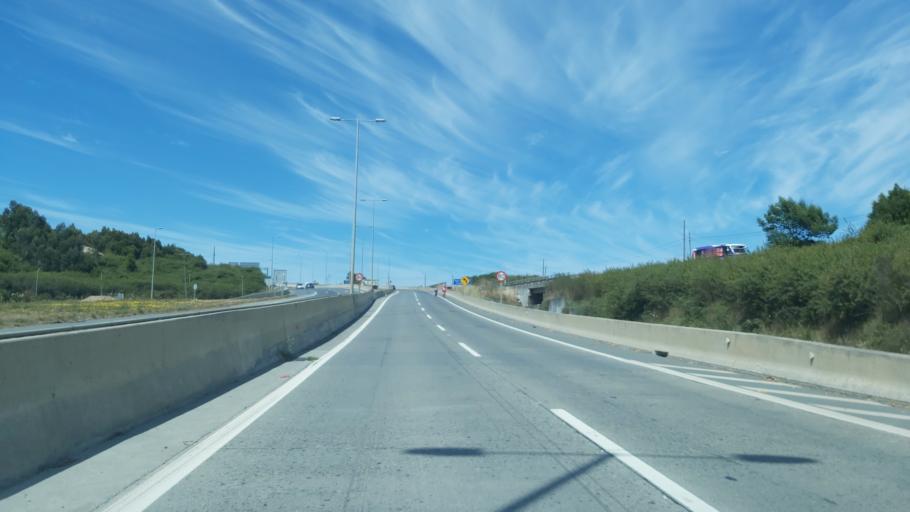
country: CL
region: Biobio
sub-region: Provincia de Concepcion
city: Coronel
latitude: -37.0447
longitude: -73.1406
